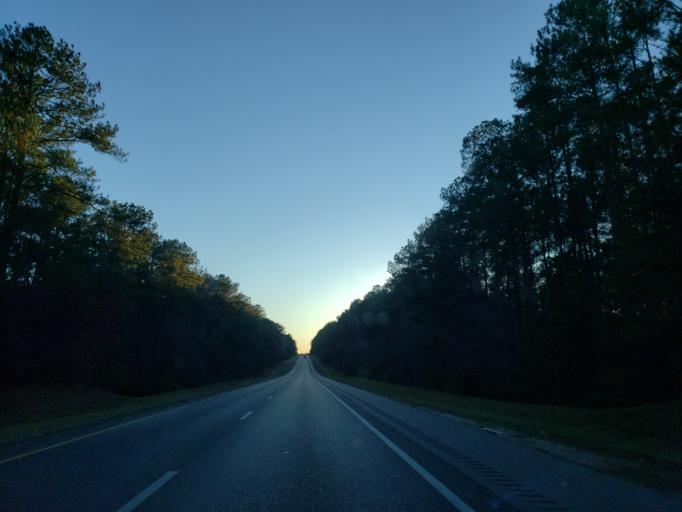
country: US
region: Mississippi
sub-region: Lauderdale County
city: Nellieburg
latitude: 32.3139
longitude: -88.7926
